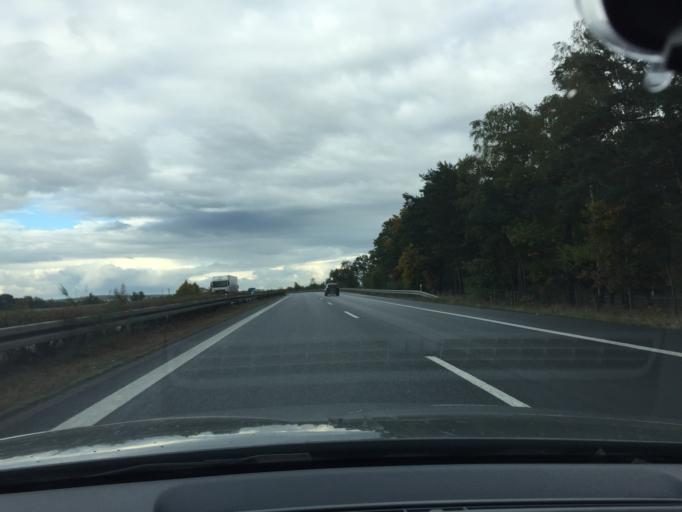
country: DE
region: Saxony
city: Thiendorf
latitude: 51.2822
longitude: 13.7315
